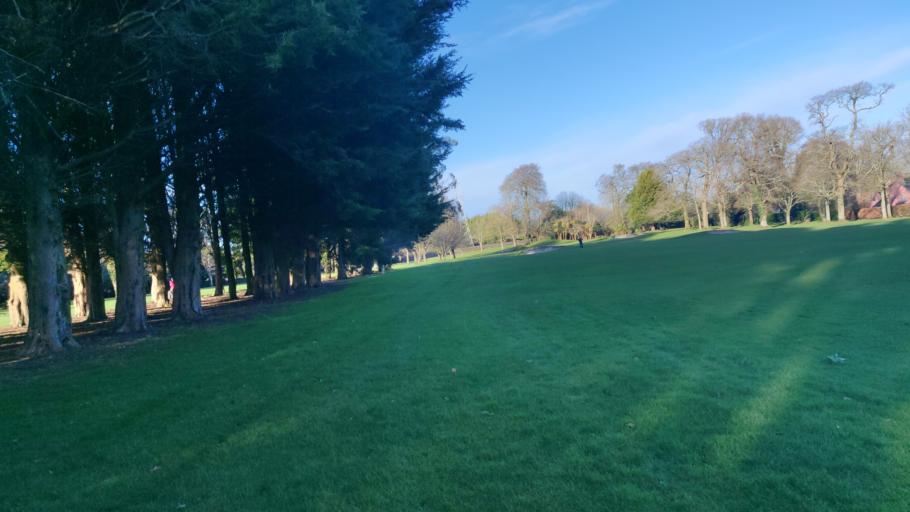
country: IE
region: Munster
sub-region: County Cork
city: Passage West
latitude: 51.8485
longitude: -8.3439
